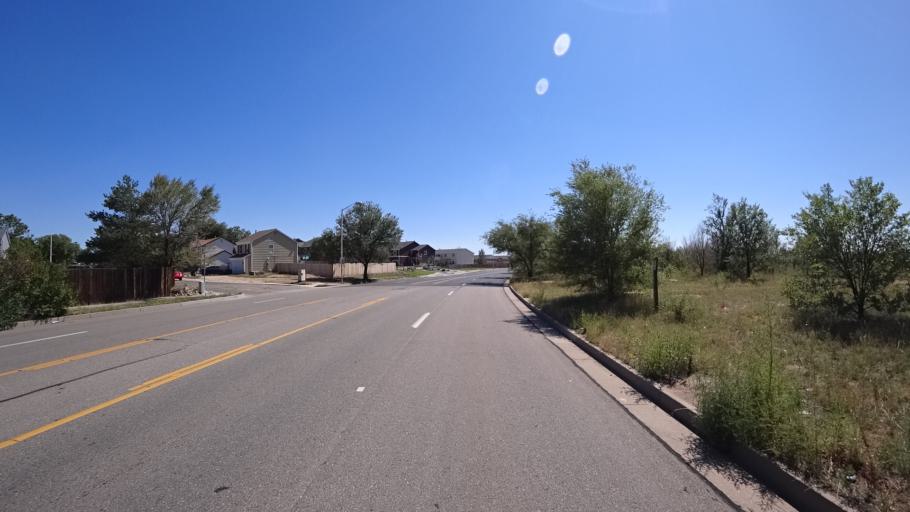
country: US
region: Colorado
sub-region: El Paso County
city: Stratmoor
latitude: 38.7909
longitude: -104.7394
